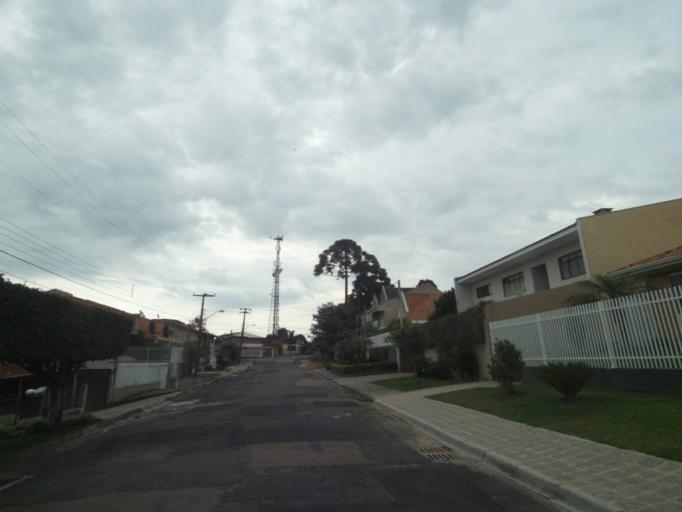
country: BR
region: Parana
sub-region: Curitiba
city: Curitiba
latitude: -25.3953
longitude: -49.2937
